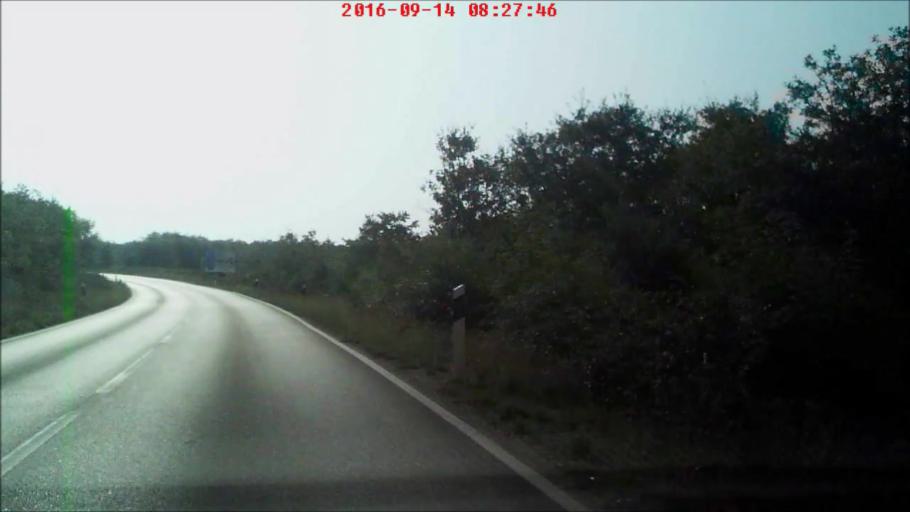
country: HR
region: Zadarska
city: Zadar
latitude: 44.1870
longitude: 15.2695
